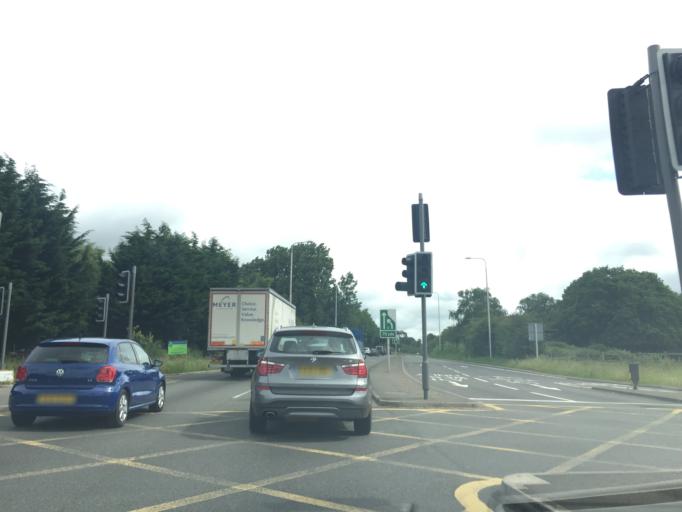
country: GB
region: England
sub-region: Dorset
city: Ferndown
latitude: 50.8027
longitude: -1.9392
